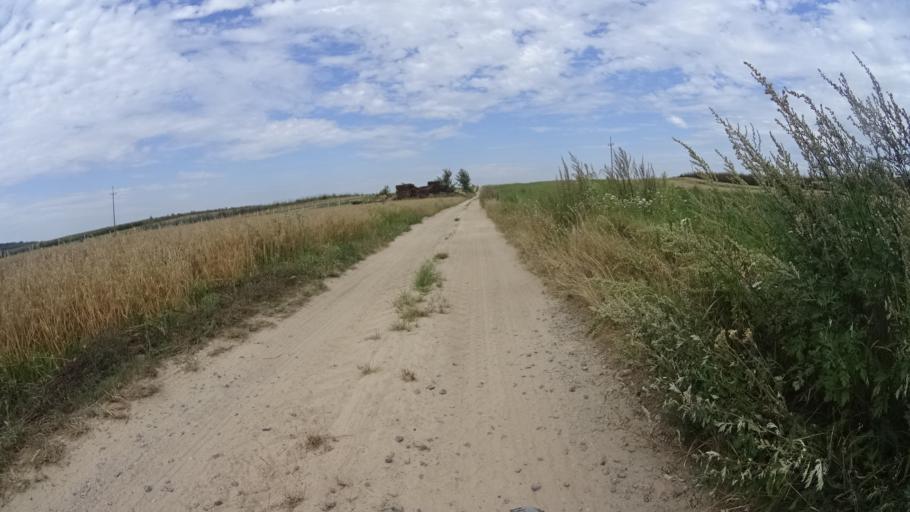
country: PL
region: Masovian Voivodeship
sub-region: Powiat bialobrzeski
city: Wysmierzyce
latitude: 51.6530
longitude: 20.8036
